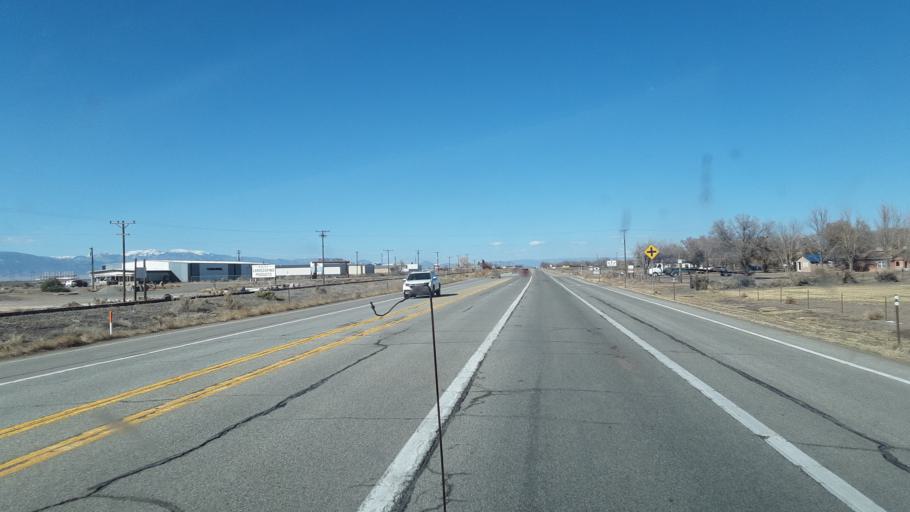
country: US
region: Colorado
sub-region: Alamosa County
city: Alamosa
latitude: 37.4895
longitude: -105.9285
